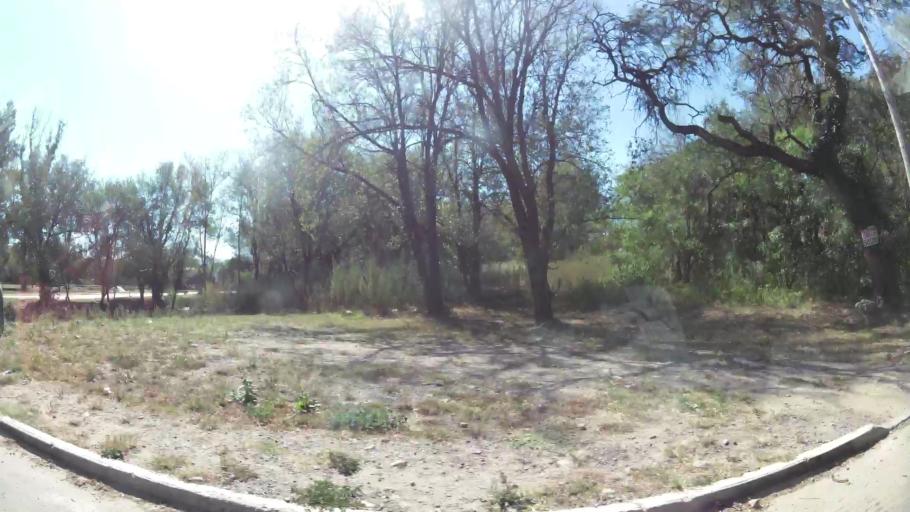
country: AR
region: Cordoba
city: Mendiolaza
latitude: -31.2690
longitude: -64.3015
